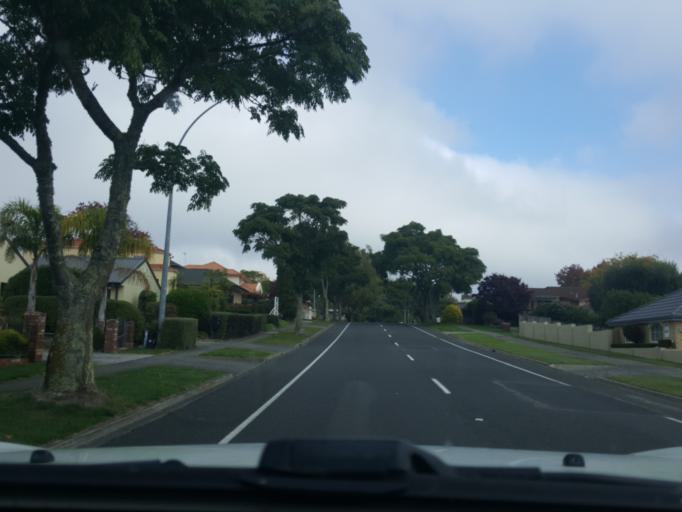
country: NZ
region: Waikato
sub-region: Hamilton City
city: Hamilton
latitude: -37.7516
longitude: 175.2924
